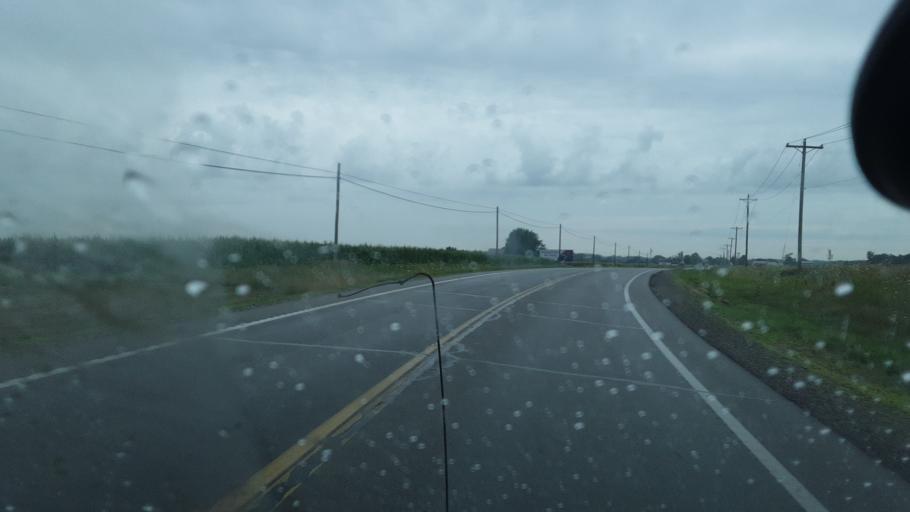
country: US
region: Ohio
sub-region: Williams County
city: Pioneer
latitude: 41.6206
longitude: -84.5534
